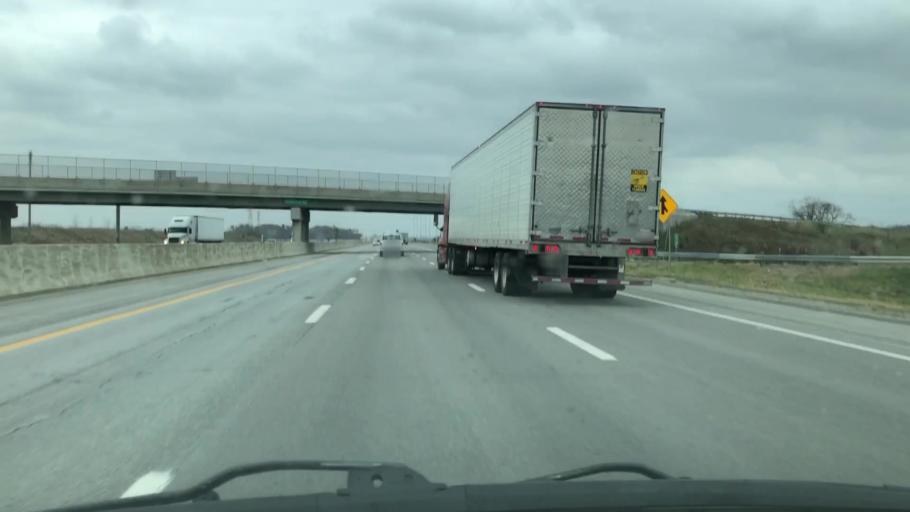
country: US
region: Ohio
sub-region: Wood County
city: Millbury
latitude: 41.5224
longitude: -83.4542
